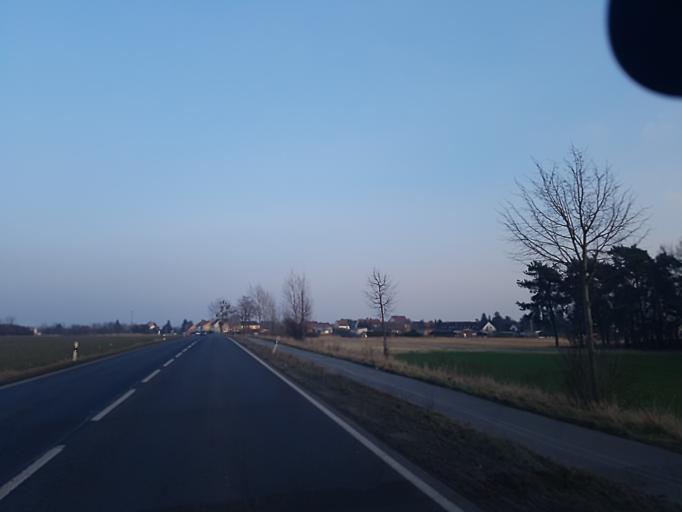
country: DE
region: Saxony-Anhalt
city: Nudersdorf
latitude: 51.8775
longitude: 12.5378
